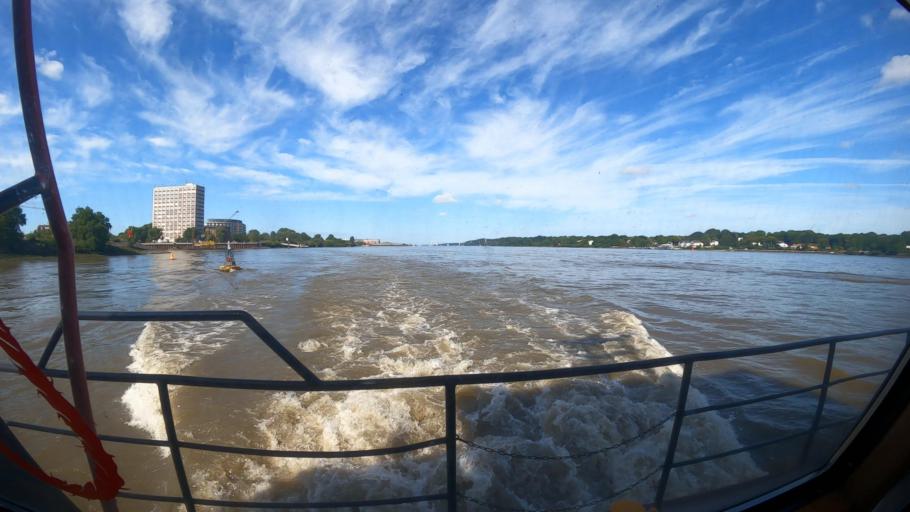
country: DE
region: Hamburg
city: Altona
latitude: 53.5418
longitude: 9.8695
